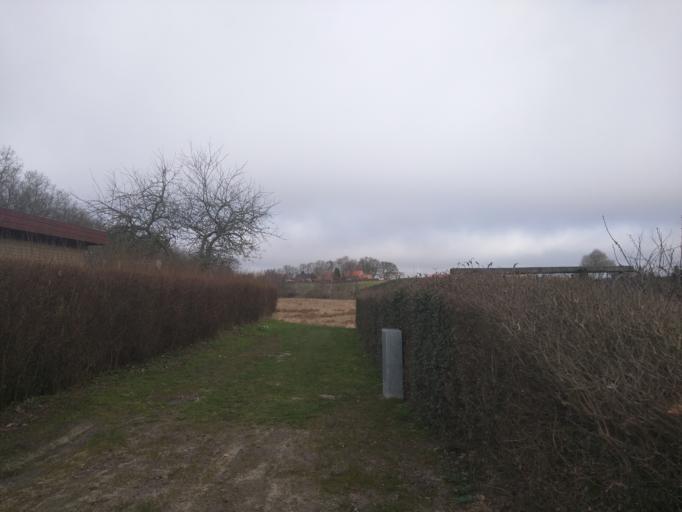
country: DK
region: Central Jutland
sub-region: Silkeborg Kommune
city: Silkeborg
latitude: 56.1942
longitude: 9.5293
